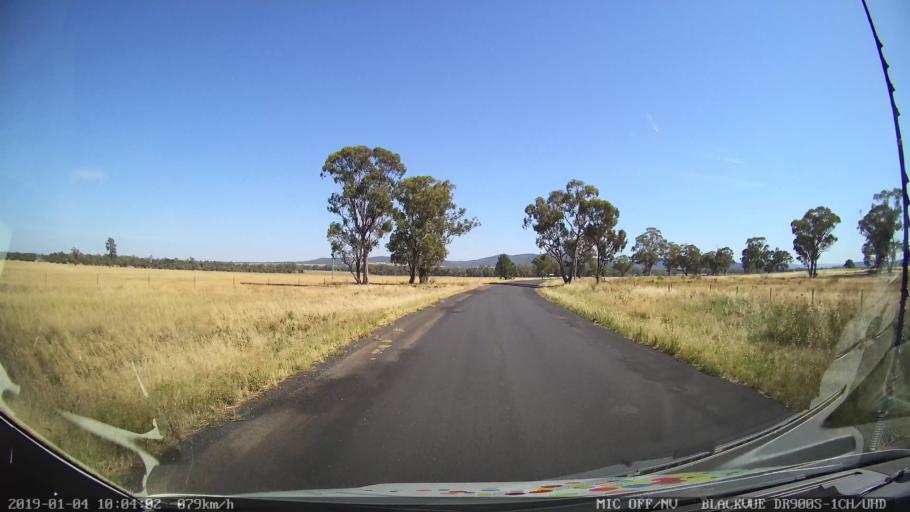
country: AU
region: New South Wales
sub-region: Cabonne
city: Canowindra
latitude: -33.4569
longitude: 148.3614
